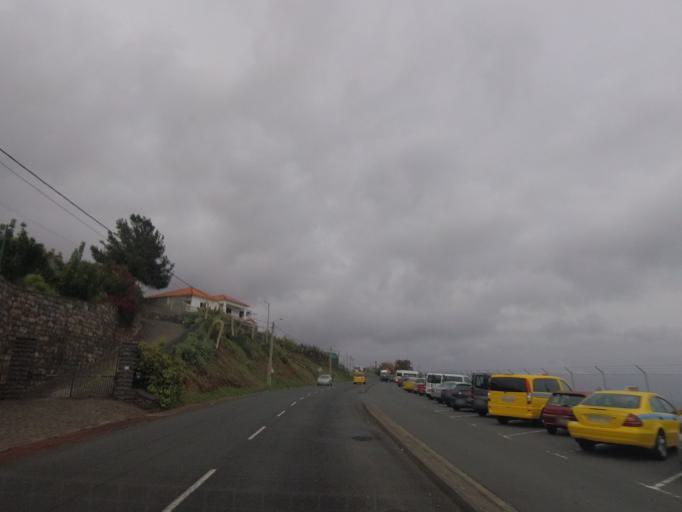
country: PT
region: Madeira
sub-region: Machico
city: Machico
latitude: 32.6935
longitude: -16.7818
